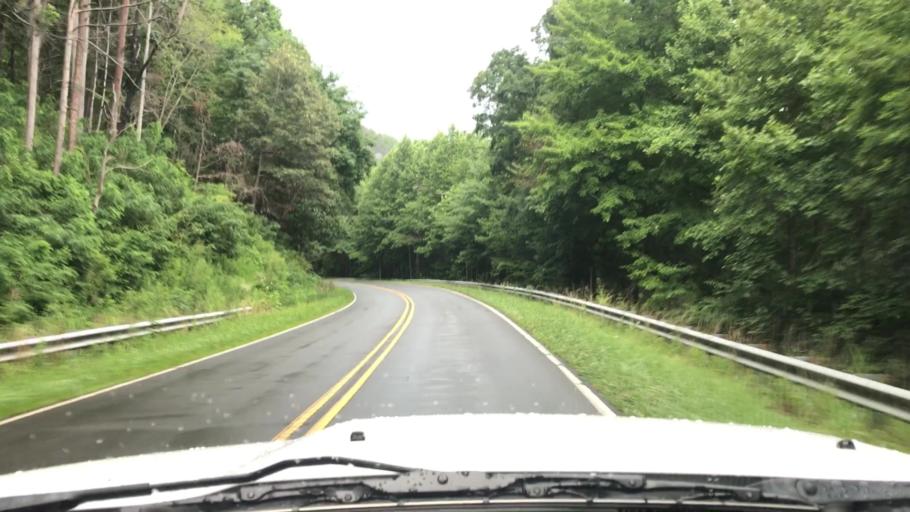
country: US
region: North Carolina
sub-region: Graham County
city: Robbinsville
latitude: 35.3691
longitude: -83.8484
